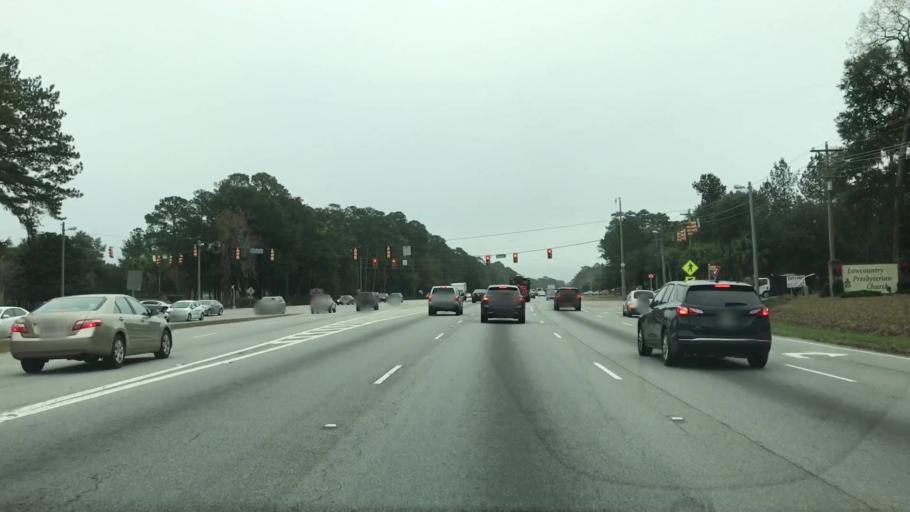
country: US
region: South Carolina
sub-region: Beaufort County
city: Bluffton
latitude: 32.2685
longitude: -80.8617
